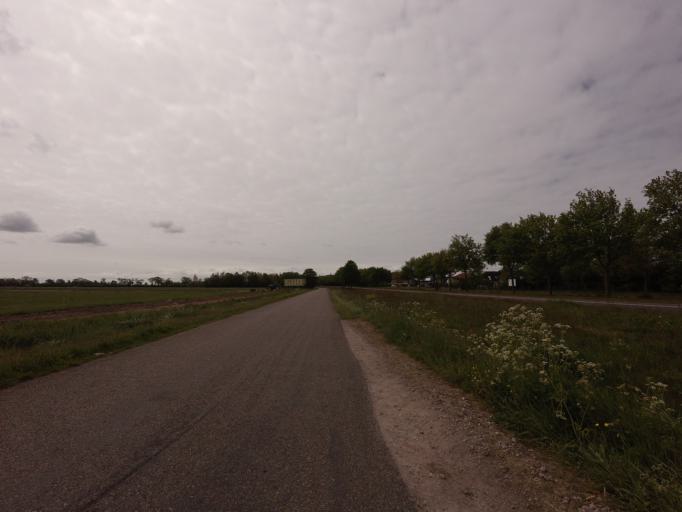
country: NL
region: Friesland
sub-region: Sudwest Fryslan
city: Koudum
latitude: 52.9131
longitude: 5.4596
